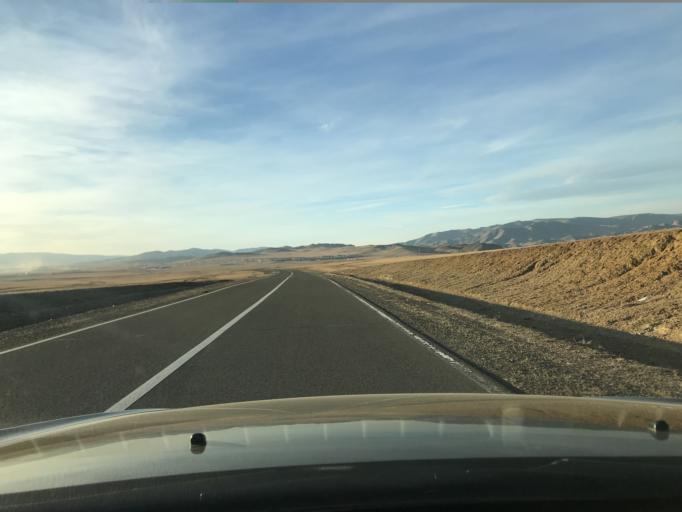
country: MN
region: Central Aimak
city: Arhust
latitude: 47.7615
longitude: 107.4386
